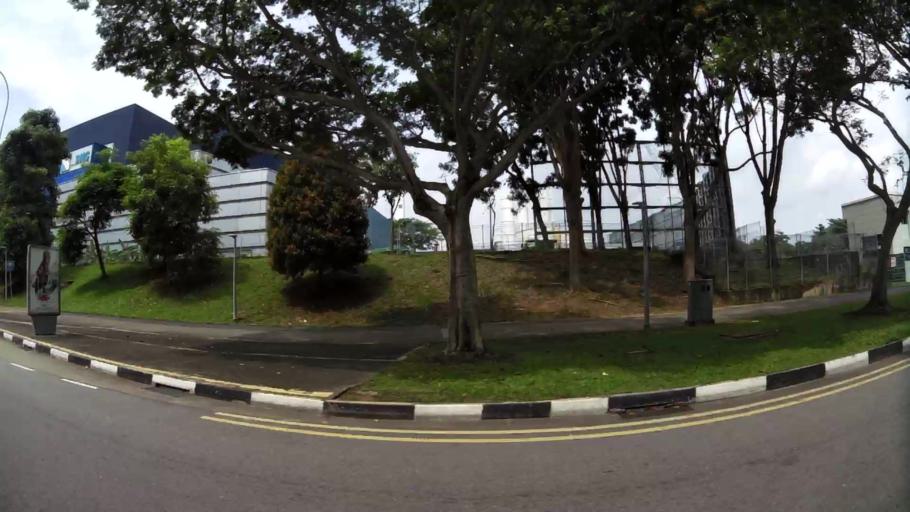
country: MY
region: Johor
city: Kampung Pasir Gudang Baru
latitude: 1.3833
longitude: 103.9361
